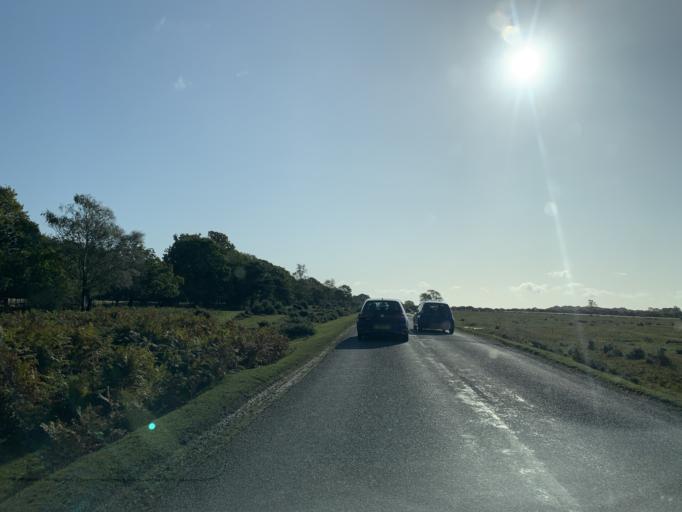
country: GB
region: England
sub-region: Wiltshire
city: Whiteparish
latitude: 50.9514
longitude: -1.6825
